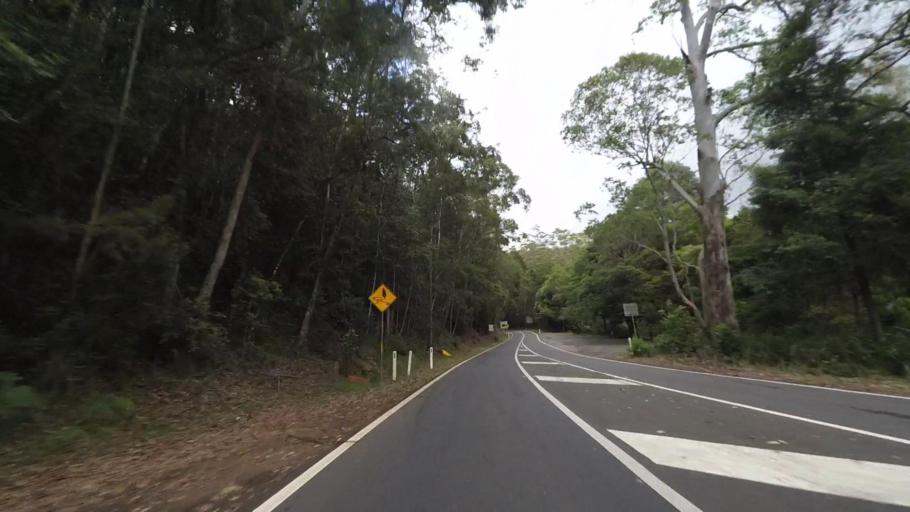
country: AU
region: New South Wales
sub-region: Wollongong
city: Helensburgh
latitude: -34.1525
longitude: 151.0290
